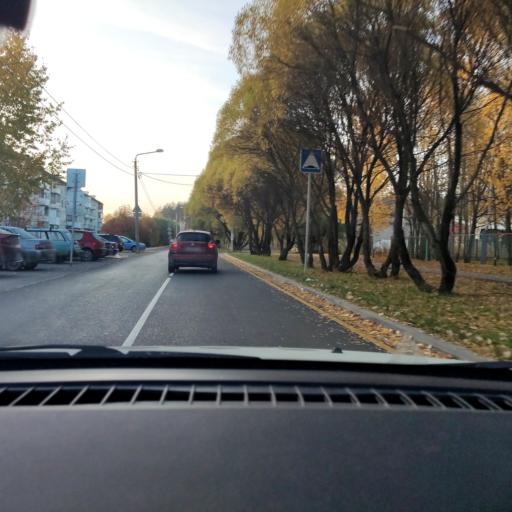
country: RU
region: Perm
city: Novyye Lyady
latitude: 58.0497
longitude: 56.5779
